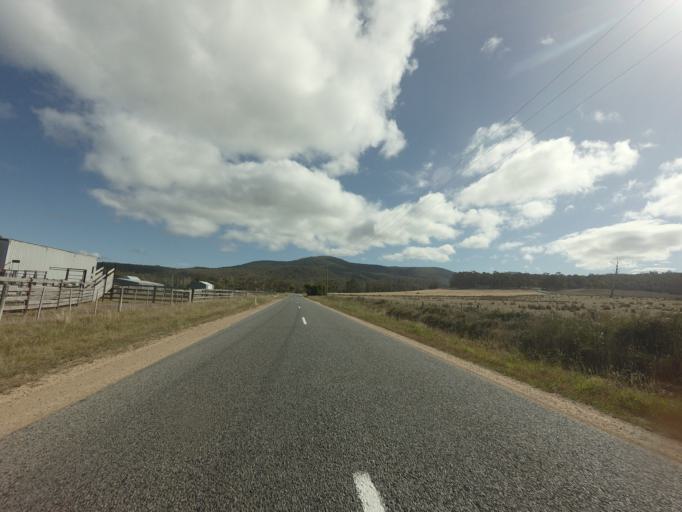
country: AU
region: Tasmania
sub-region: Break O'Day
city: St Helens
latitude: -41.7754
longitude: 148.2621
